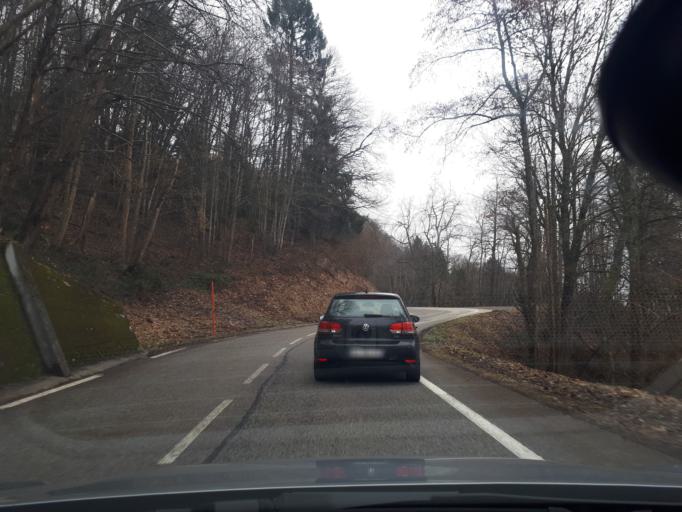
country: FR
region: Rhone-Alpes
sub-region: Departement de l'Isere
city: Vaulnaveys-le-Bas
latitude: 45.1199
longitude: 5.8371
